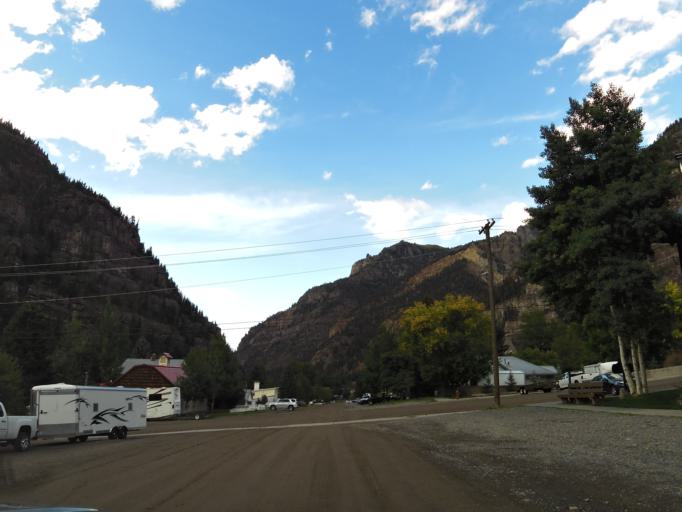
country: US
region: Colorado
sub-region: Ouray County
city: Ouray
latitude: 38.0213
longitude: -107.6729
